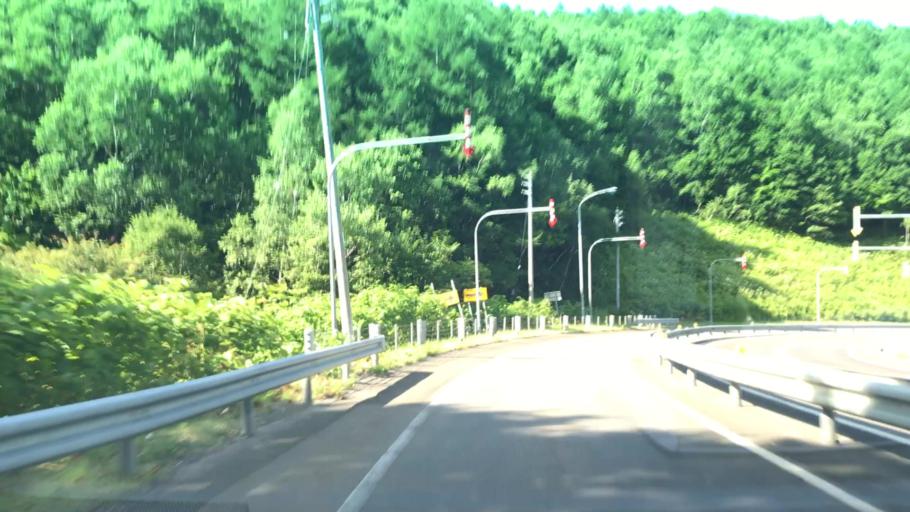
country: JP
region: Hokkaido
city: Yoichi
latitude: 43.0638
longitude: 140.6940
